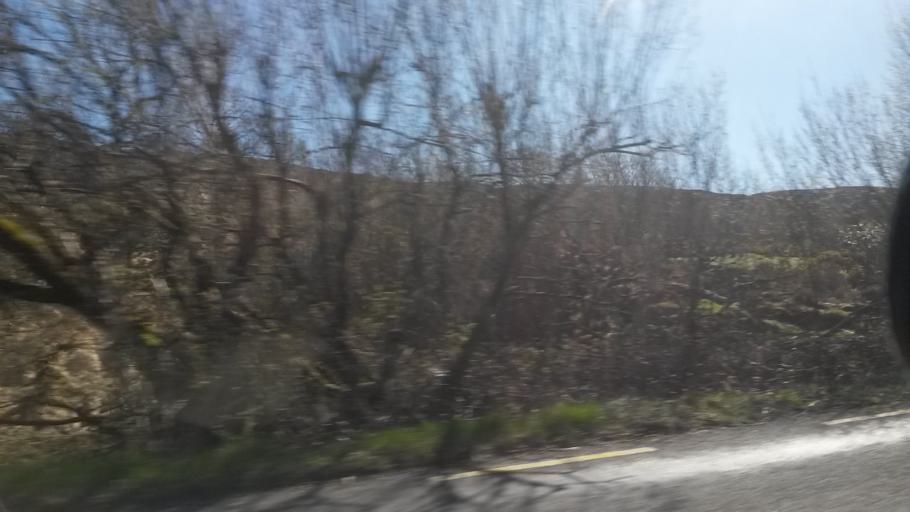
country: IE
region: Munster
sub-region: Ciarrai
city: Cill Airne
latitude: 51.9413
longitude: -9.3834
